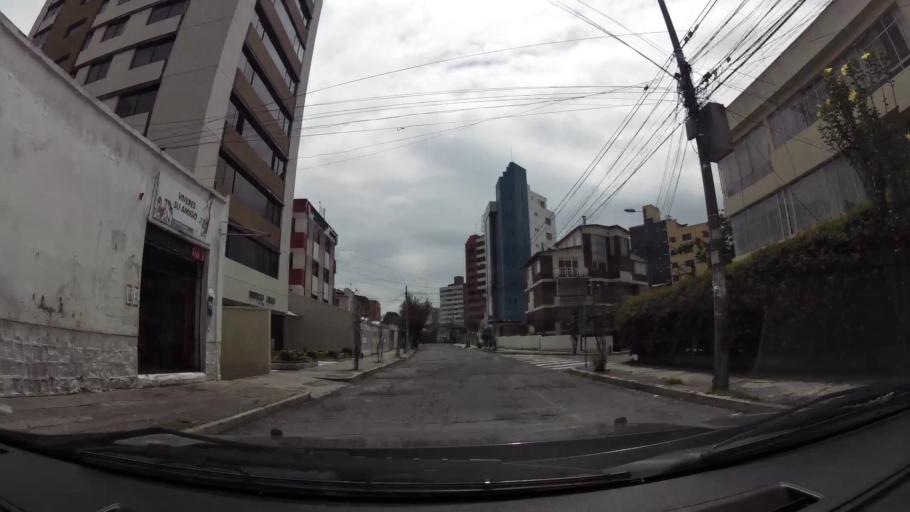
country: EC
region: Pichincha
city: Quito
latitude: -0.1851
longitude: -78.4902
